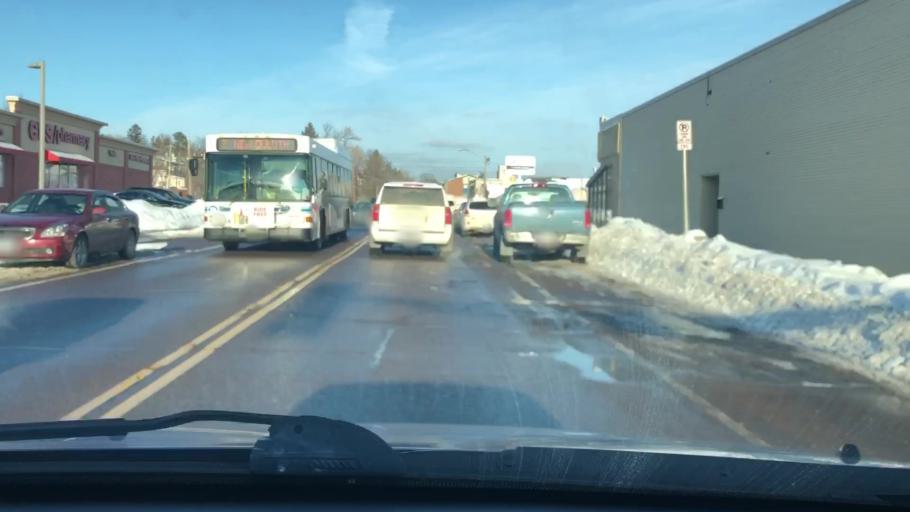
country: US
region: Minnesota
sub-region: Saint Louis County
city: Duluth
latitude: 46.7985
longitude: -92.0830
